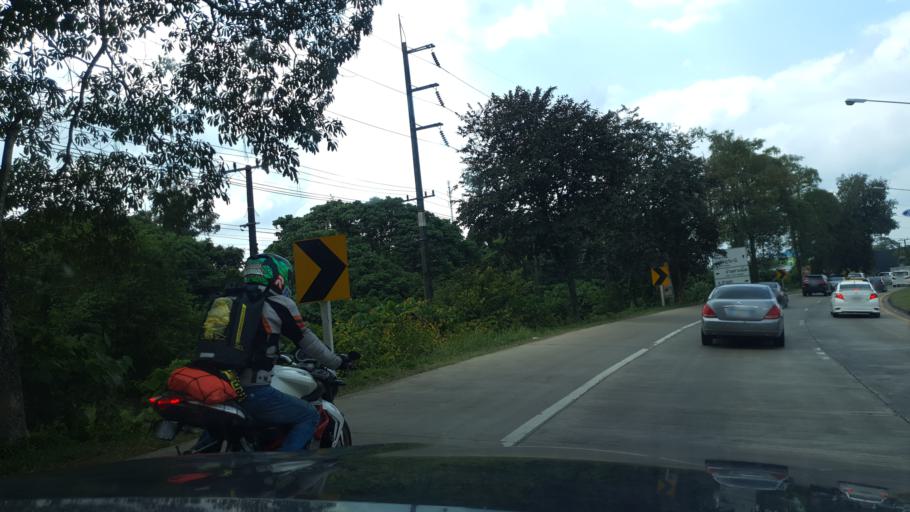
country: TH
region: Chumphon
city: Tha Sae
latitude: 10.6640
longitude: 99.2014
